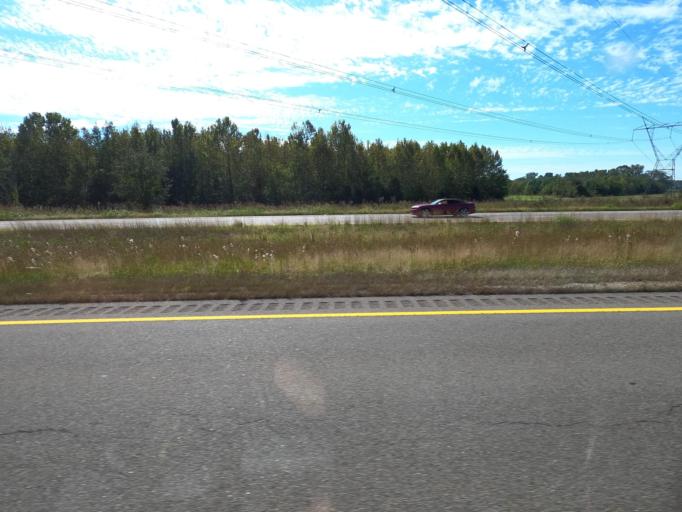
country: US
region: Tennessee
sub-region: Madison County
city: Three Way
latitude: 35.6716
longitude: -88.9461
